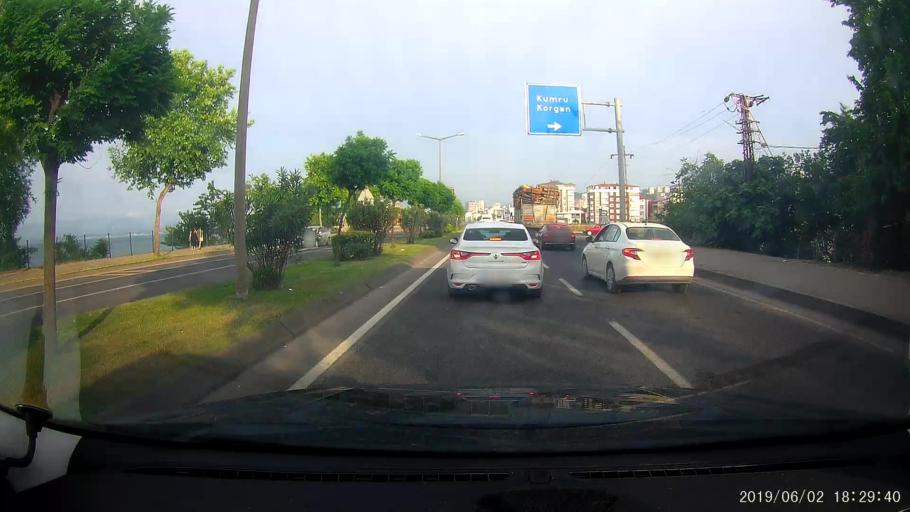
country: TR
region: Ordu
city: Fatsa
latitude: 41.0384
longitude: 37.4911
